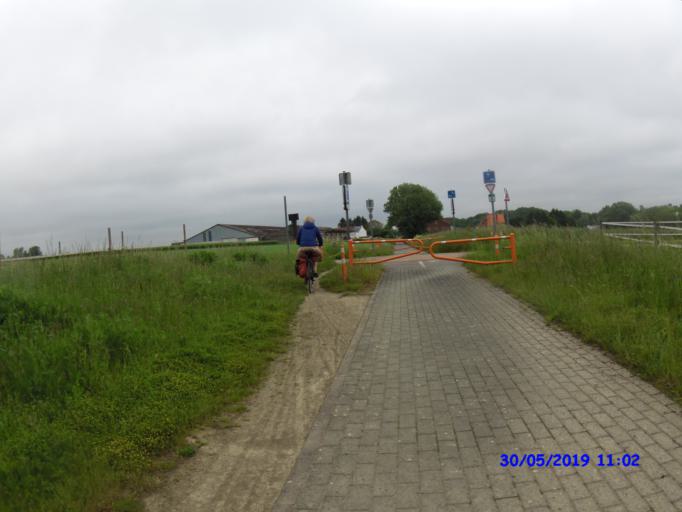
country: BE
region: Wallonia
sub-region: Province du Hainaut
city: Thuin
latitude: 50.2789
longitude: 4.3144
